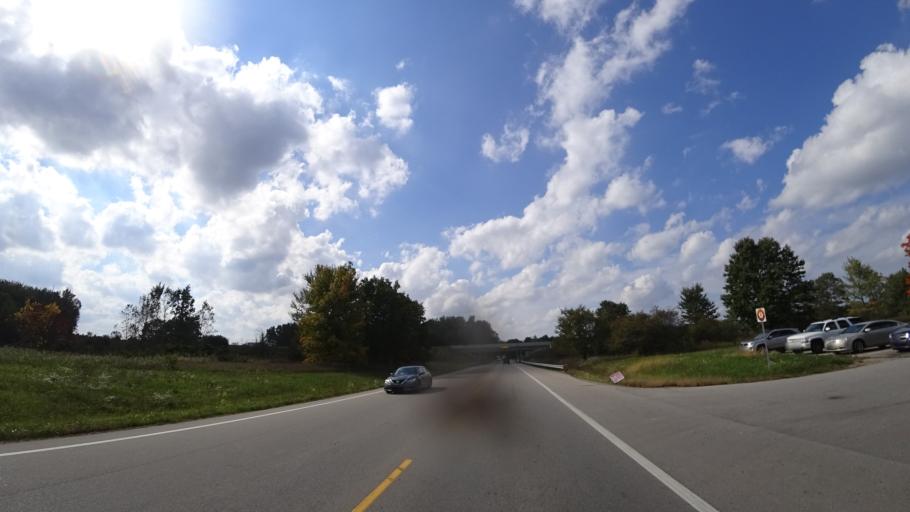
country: US
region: Michigan
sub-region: Branch County
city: Union City
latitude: 42.1058
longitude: -84.9940
